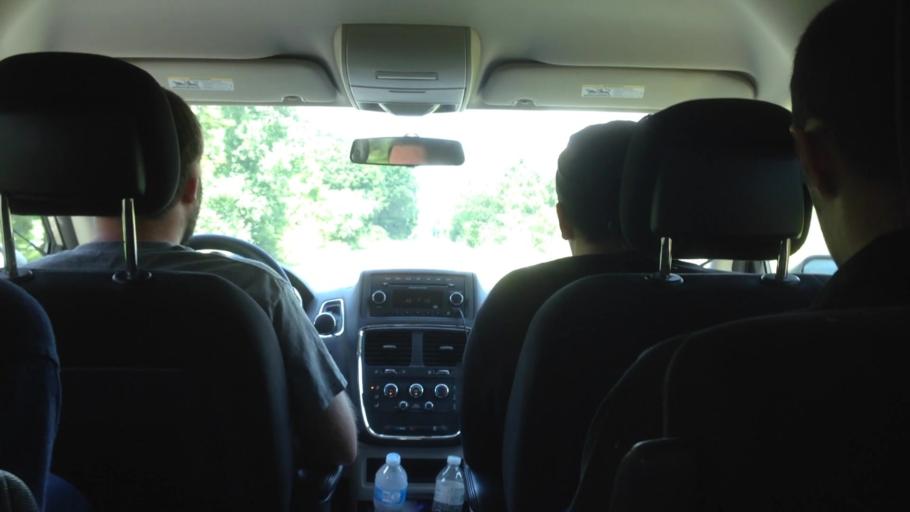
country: US
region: New York
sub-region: Dutchess County
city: Tivoli
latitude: 42.1092
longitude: -73.8938
